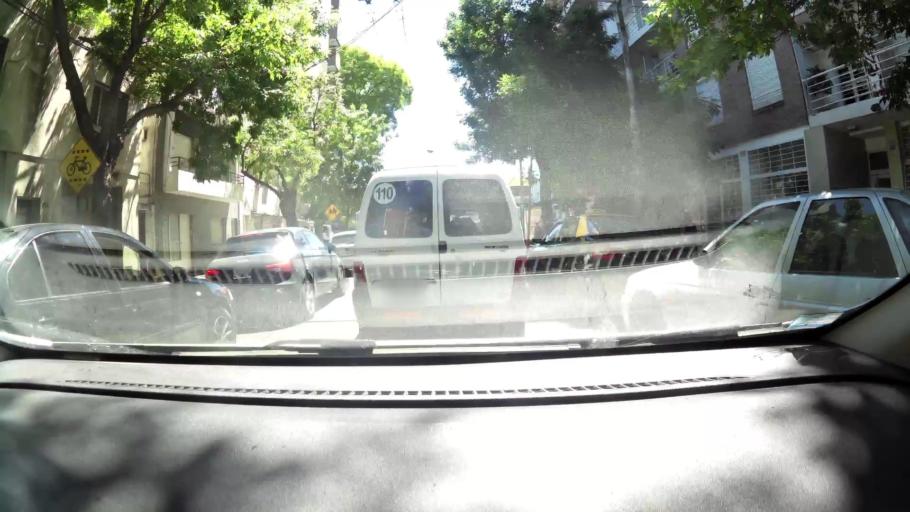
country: AR
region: Santa Fe
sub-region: Departamento de Rosario
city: Rosario
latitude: -32.9454
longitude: -60.6659
